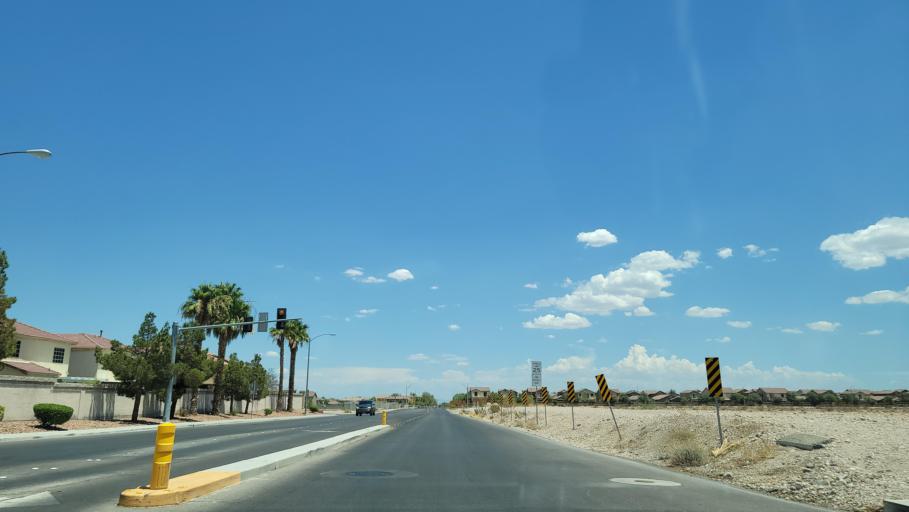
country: US
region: Nevada
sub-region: Clark County
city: Spring Valley
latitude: 36.0777
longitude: -115.2737
